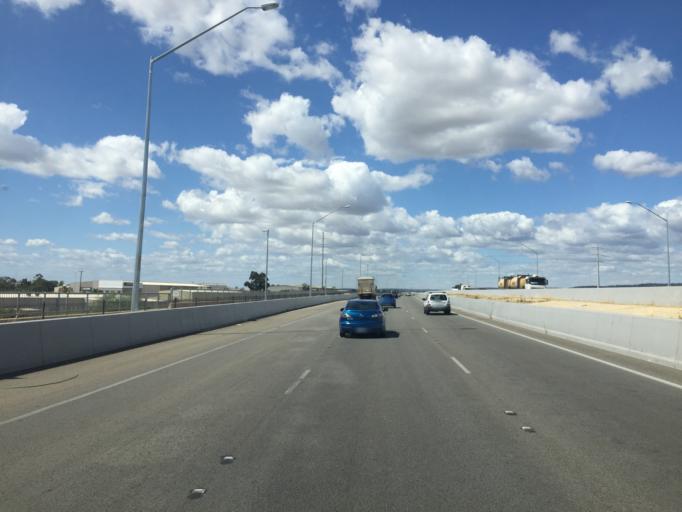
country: AU
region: Western Australia
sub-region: Canning
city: East Cannington
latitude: -31.9995
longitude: 115.9761
